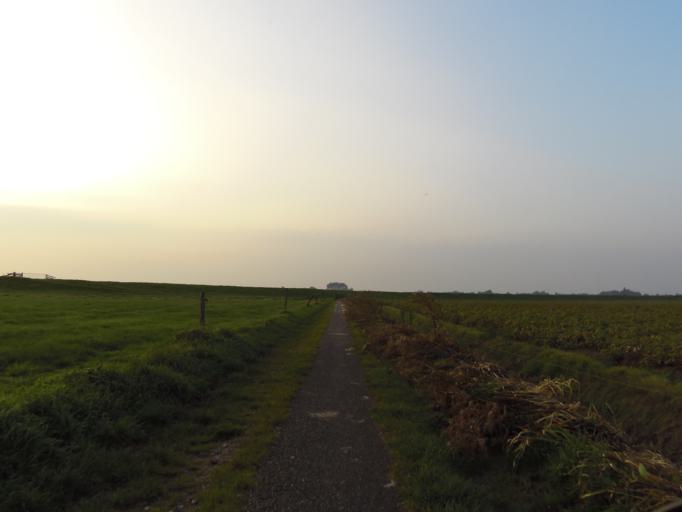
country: NL
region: South Holland
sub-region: Gemeente Rijnwoude
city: Benthuizen
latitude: 52.0970
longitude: 4.5282
